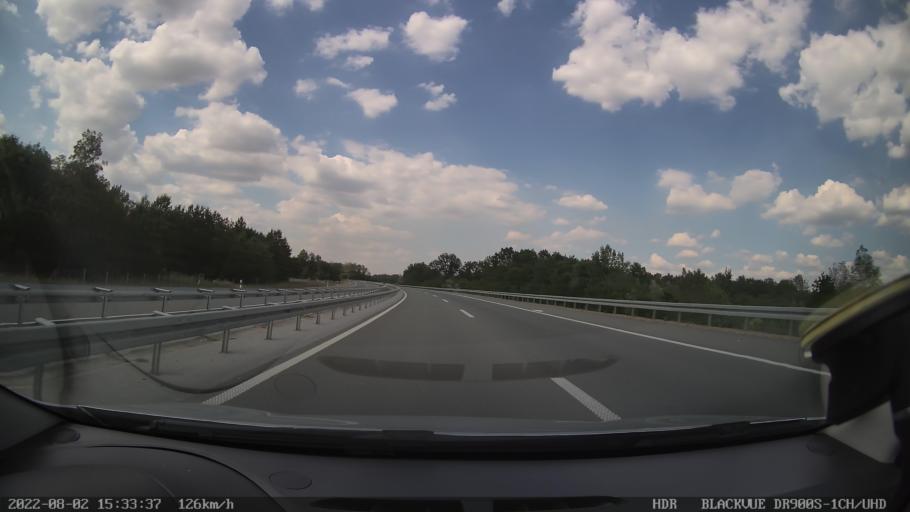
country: RS
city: Stubline
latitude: 44.5015
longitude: 20.1497
